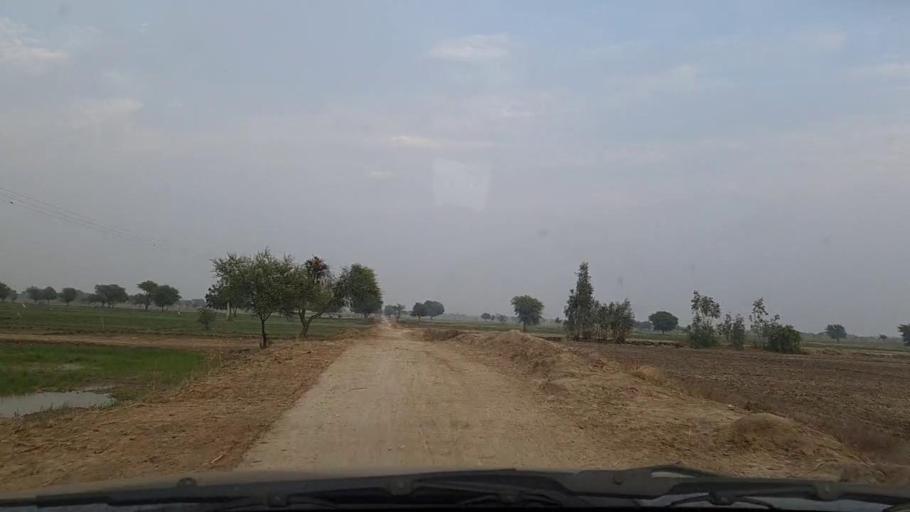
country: PK
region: Sindh
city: Dhoro Naro
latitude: 25.5931
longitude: 69.4959
